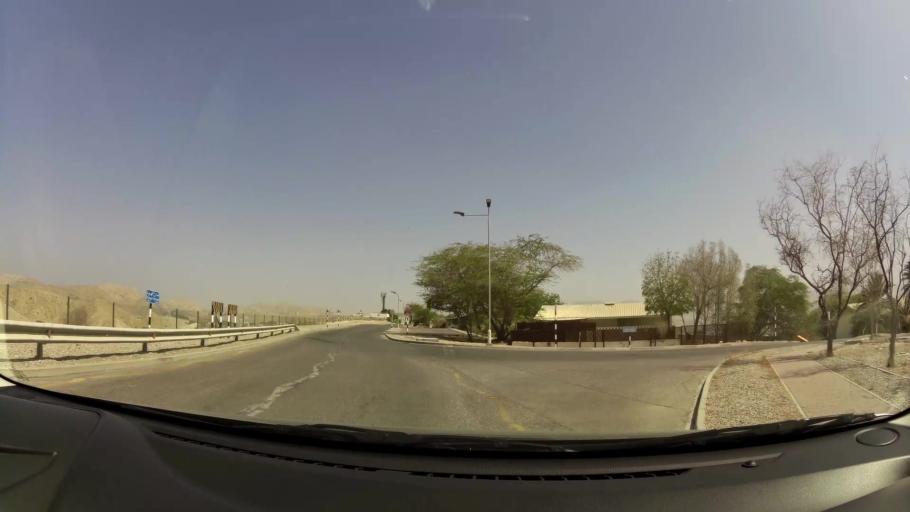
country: OM
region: Muhafazat Masqat
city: Muscat
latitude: 23.6308
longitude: 58.4999
